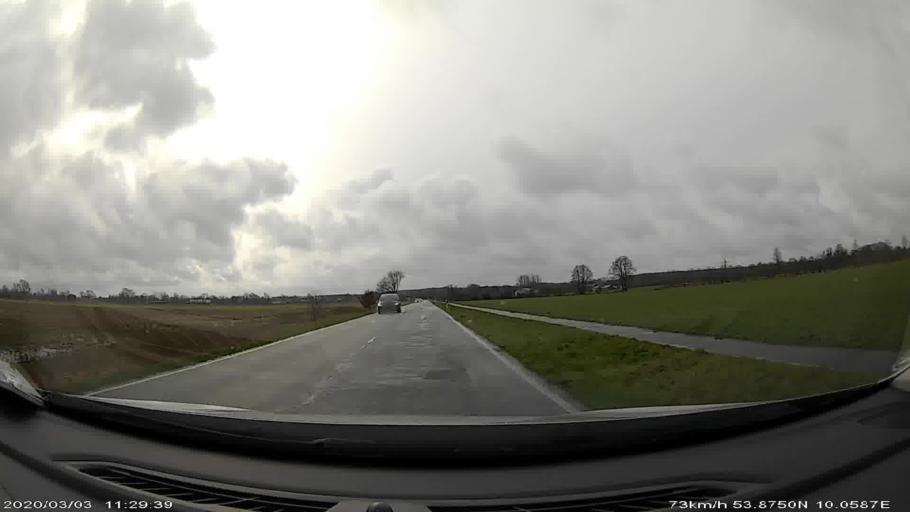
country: DE
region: Schleswig-Holstein
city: Struvenhutten
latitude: 53.8721
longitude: 10.0579
